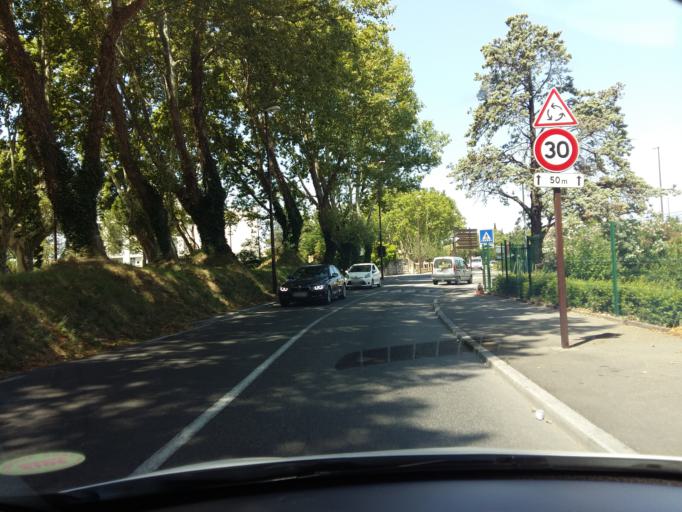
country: FR
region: Provence-Alpes-Cote d'Azur
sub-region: Departement du Vaucluse
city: Avignon
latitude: 43.9467
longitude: 4.8294
